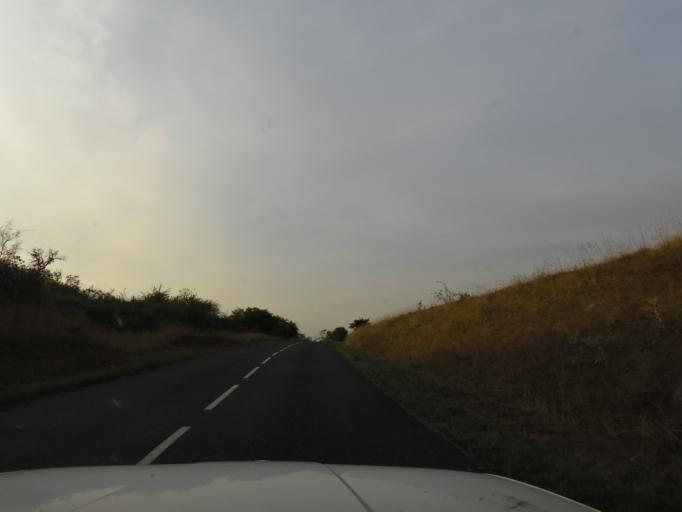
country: FR
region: Rhone-Alpes
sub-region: Departement de l'Ain
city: Saint-Maurice-de-Gourdans
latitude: 45.8530
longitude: 5.1858
